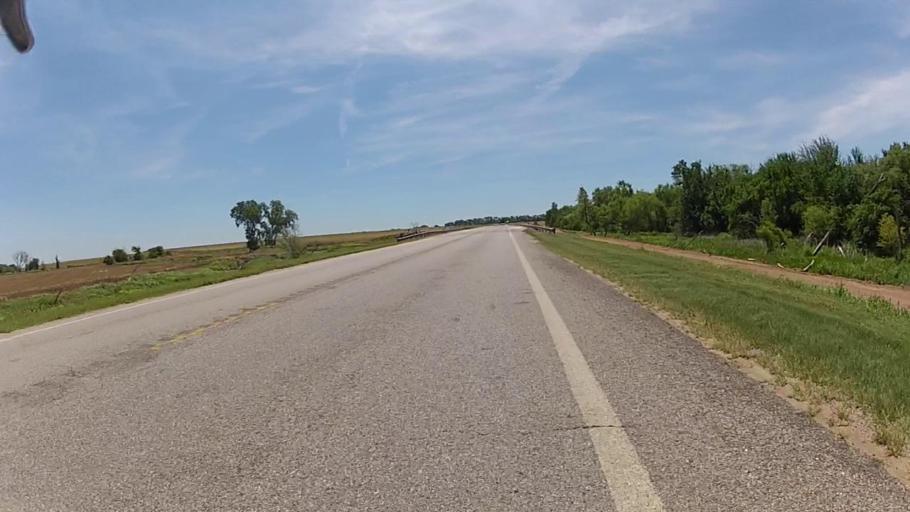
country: US
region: Kansas
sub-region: Barber County
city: Medicine Lodge
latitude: 37.2615
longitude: -98.5294
